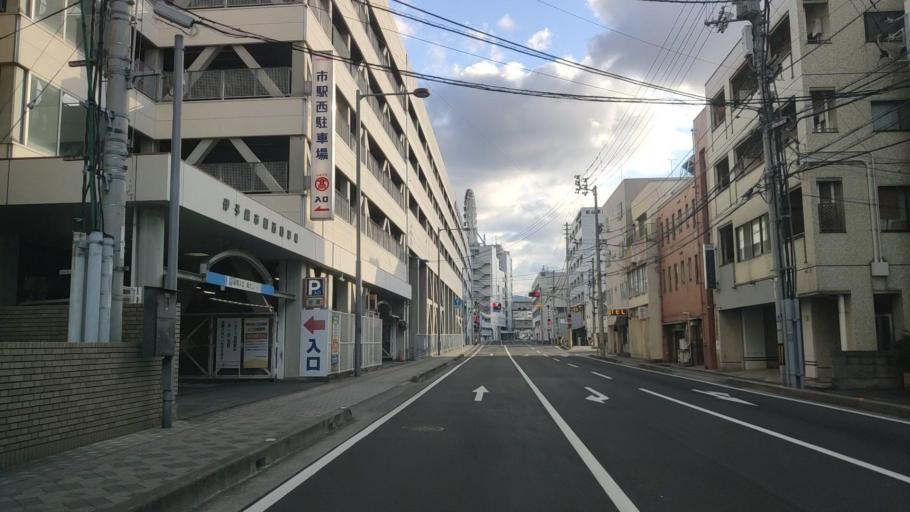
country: JP
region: Ehime
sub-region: Shikoku-chuo Shi
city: Matsuyama
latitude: 33.8352
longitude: 132.7591
